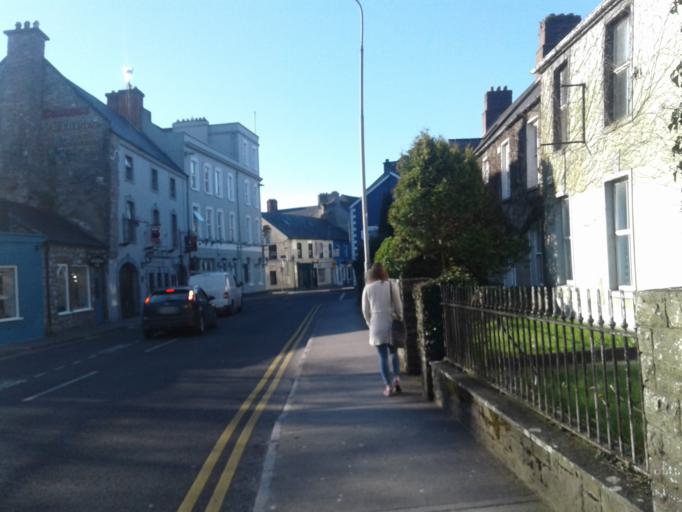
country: IE
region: Munster
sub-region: An Clar
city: Ennis
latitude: 52.8459
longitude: -8.9818
